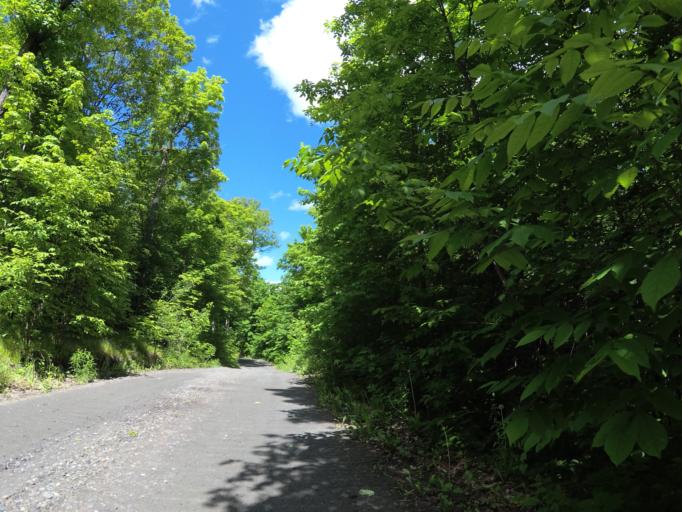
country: CA
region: Ontario
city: Renfrew
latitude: 45.0560
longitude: -76.8369
